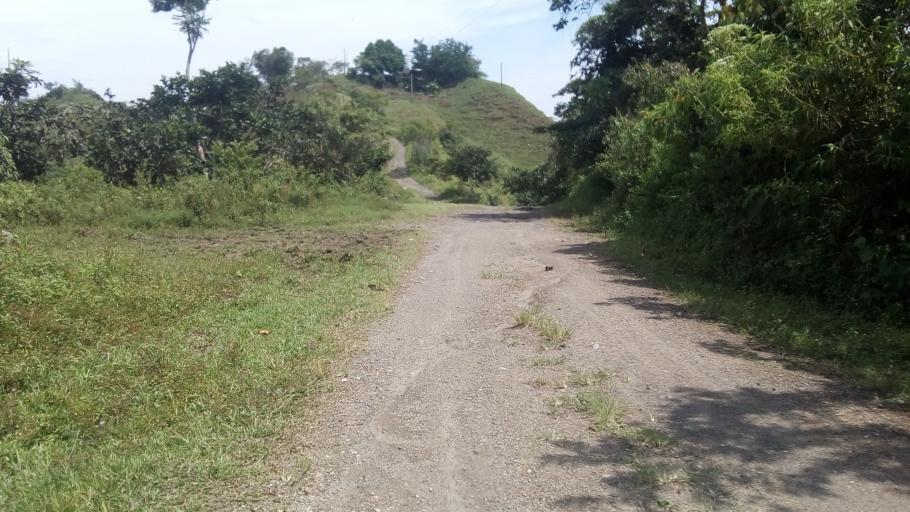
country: CO
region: Boyaca
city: Otanche
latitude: 5.6231
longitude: -74.2335
